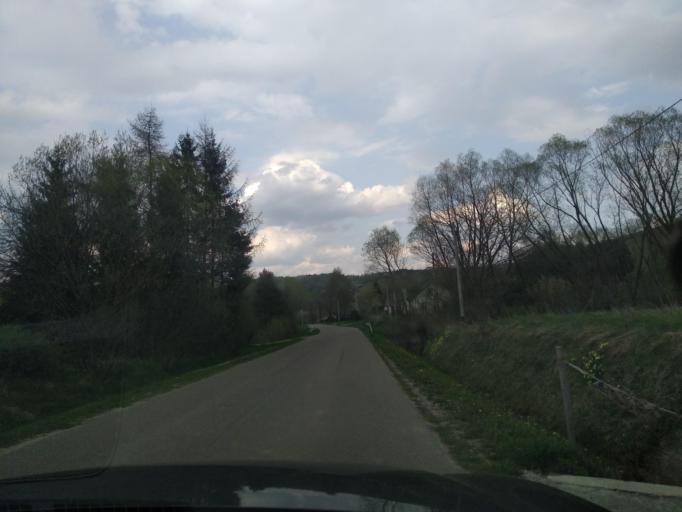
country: PL
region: Subcarpathian Voivodeship
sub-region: Powiat sanocki
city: Czaszyn
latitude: 49.4007
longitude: 22.2221
